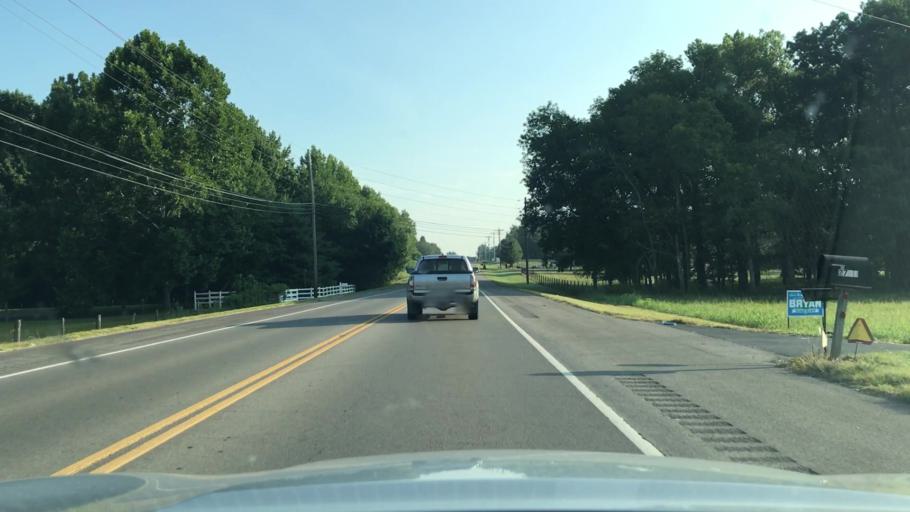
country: US
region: Tennessee
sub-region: Wilson County
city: Rural Hill
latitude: 36.1322
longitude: -86.5194
